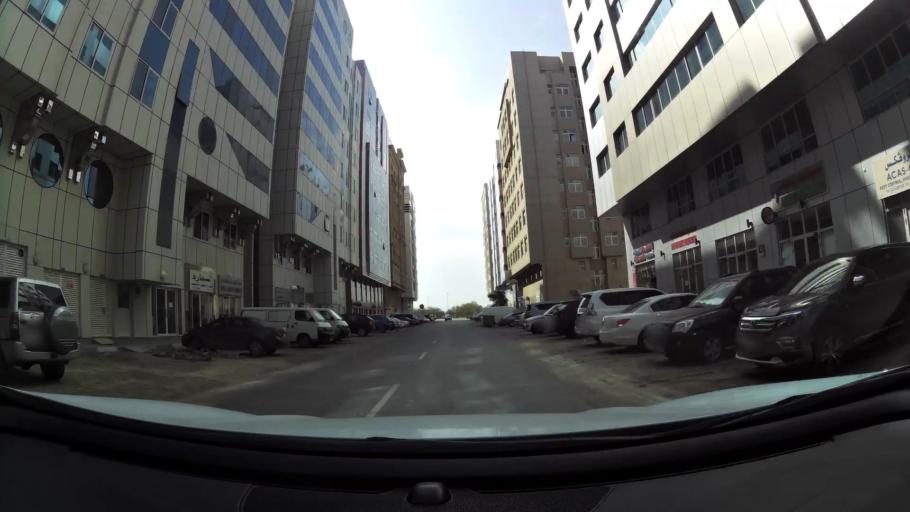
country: AE
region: Abu Dhabi
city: Abu Dhabi
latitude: 24.3410
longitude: 54.5323
